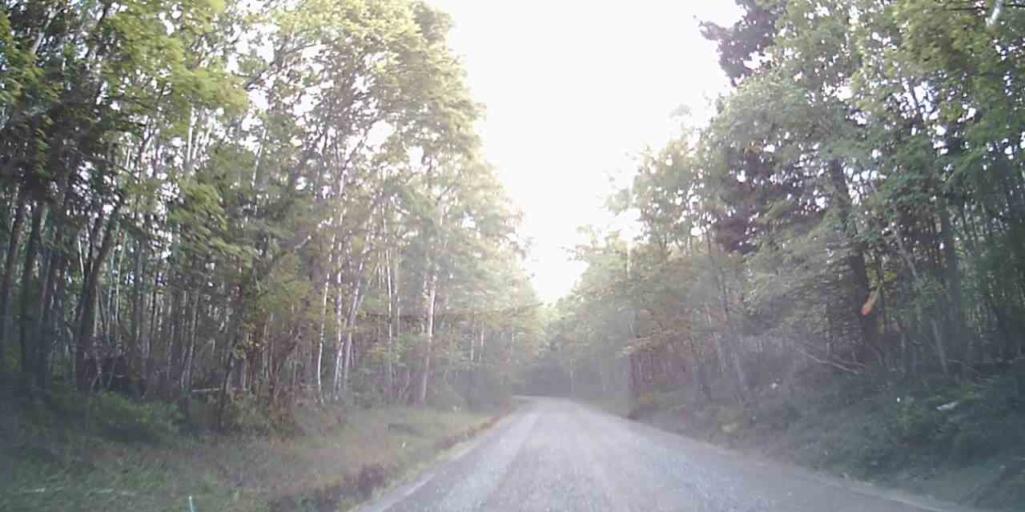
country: JP
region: Hokkaido
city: Shiraoi
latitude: 42.7104
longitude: 141.3992
